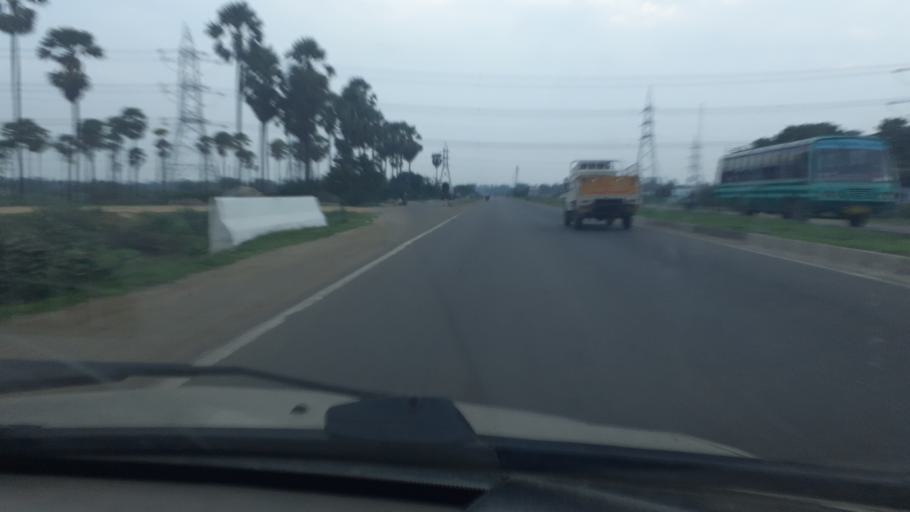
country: IN
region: Tamil Nadu
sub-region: Thoothukkudi
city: Korampallam
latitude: 8.7730
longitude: 78.0848
